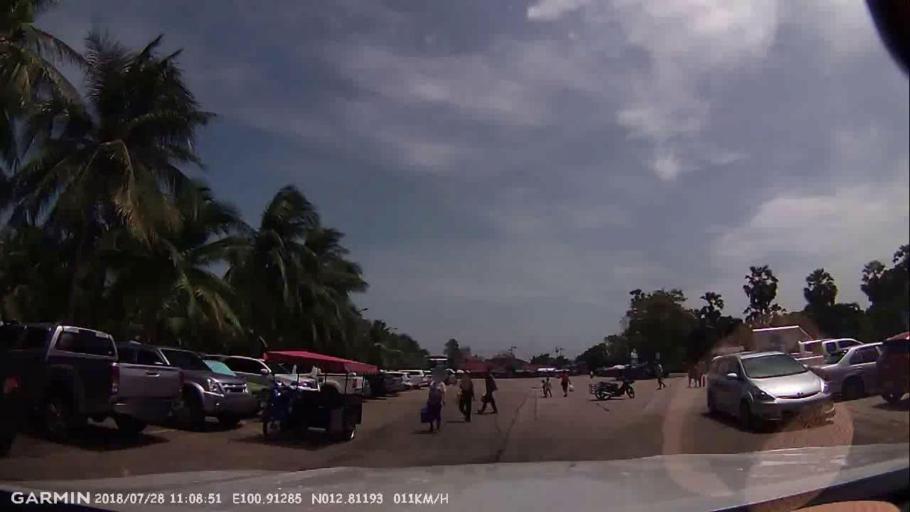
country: TH
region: Chon Buri
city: Phatthaya
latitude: 12.8119
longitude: 100.9128
